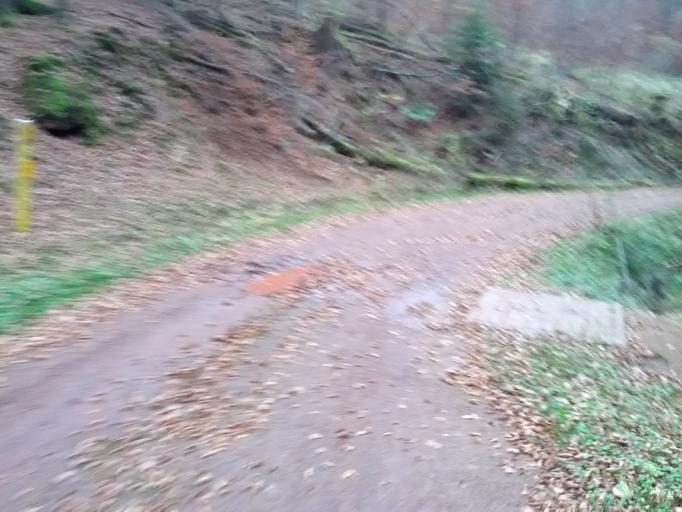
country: DE
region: Thuringia
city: Eisenach
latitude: 50.9443
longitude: 10.3072
